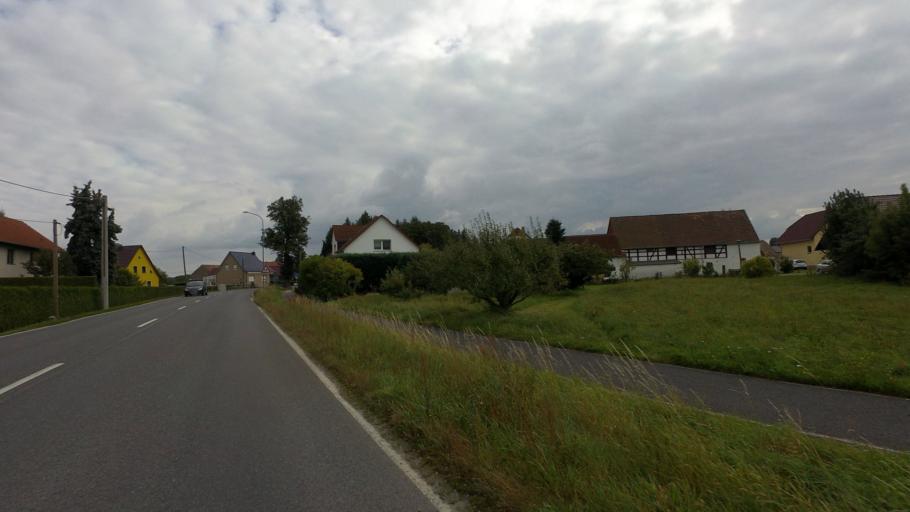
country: DE
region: Saxony
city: Konigswartha
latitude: 51.3522
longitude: 14.3256
